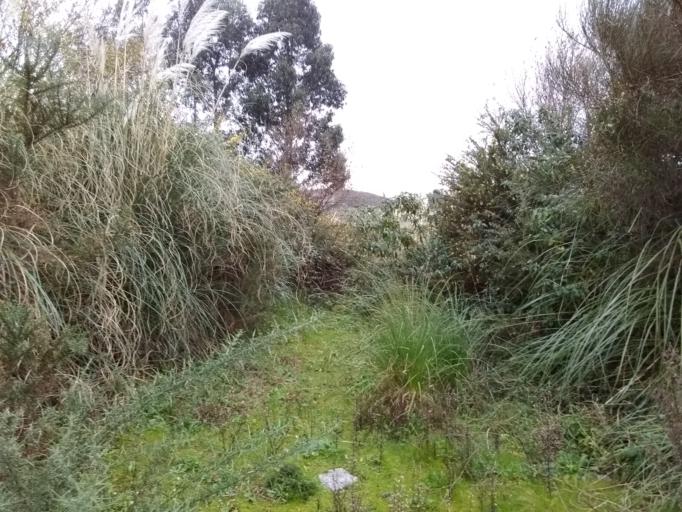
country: ES
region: Galicia
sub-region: Provincia da Coruna
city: A Coruna
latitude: 43.3304
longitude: -8.4405
